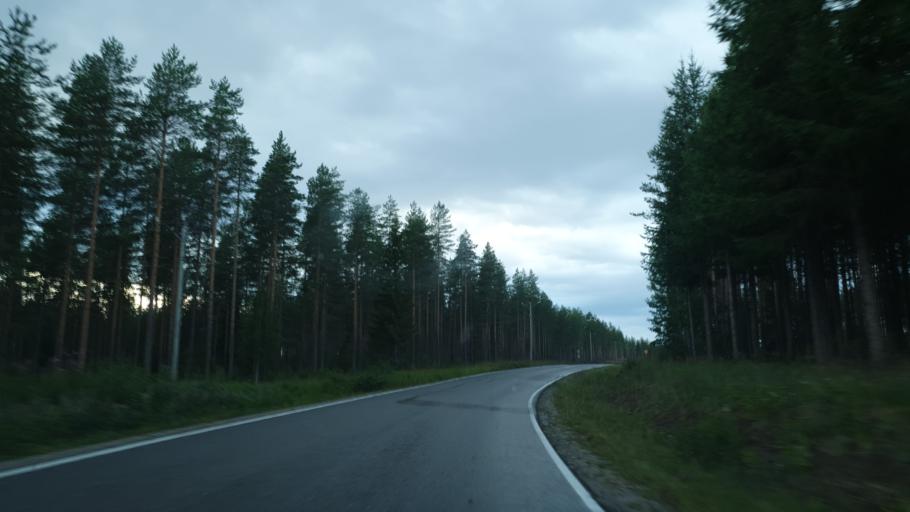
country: FI
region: North Karelia
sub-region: Pielisen Karjala
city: Lieksa
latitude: 63.5371
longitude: 29.9772
